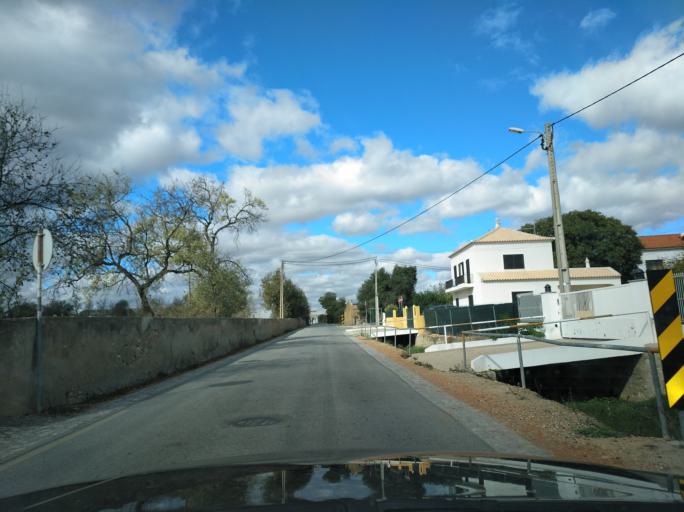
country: PT
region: Faro
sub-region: Tavira
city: Luz
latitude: 37.0942
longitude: -7.7043
